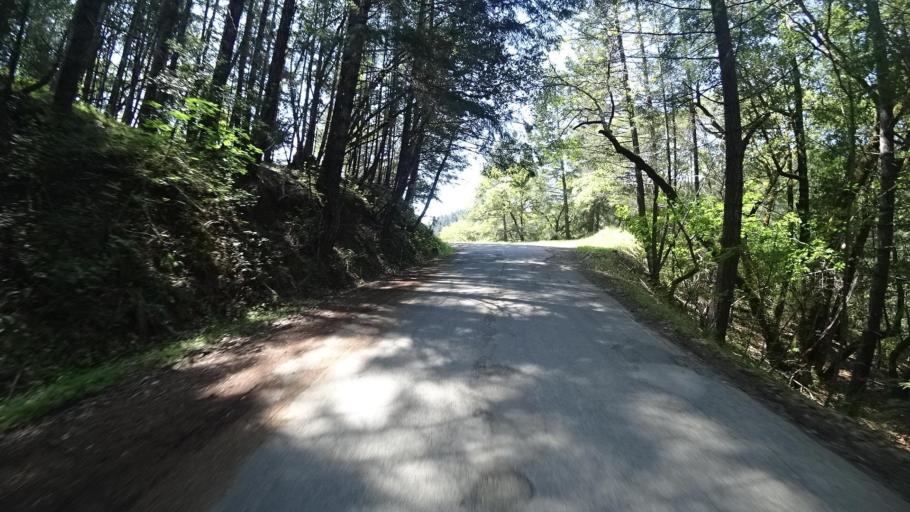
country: US
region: California
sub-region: Humboldt County
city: Redway
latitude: 40.1991
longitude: -123.5202
